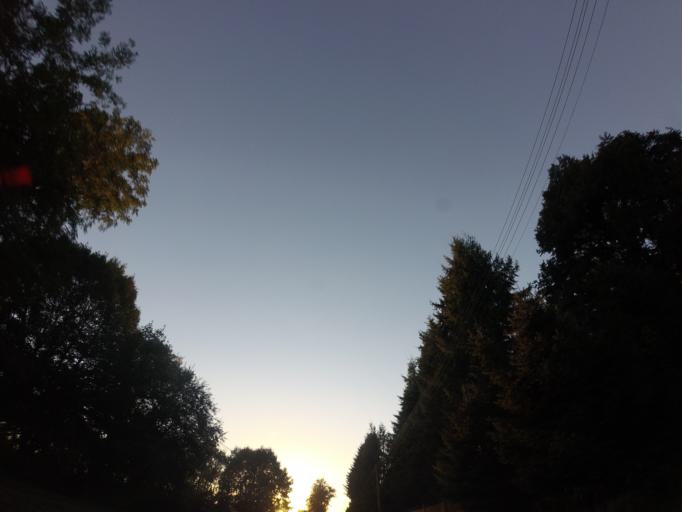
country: PL
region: Lubusz
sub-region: Powiat strzelecko-drezdenecki
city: Drezdenko
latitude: 52.8546
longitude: 15.8209
